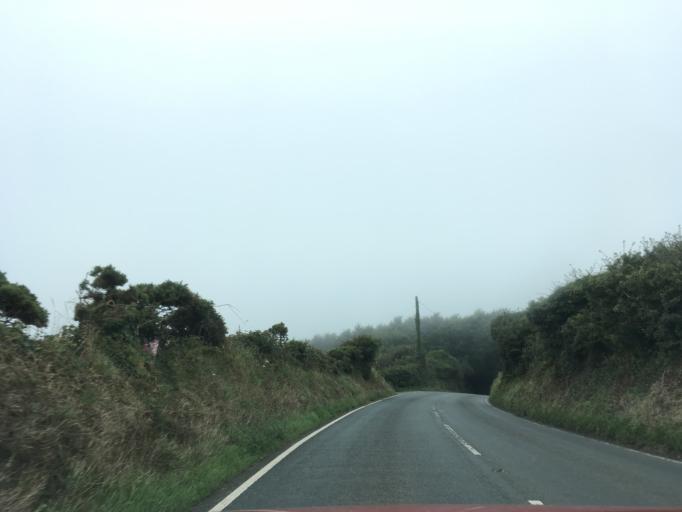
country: GB
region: Wales
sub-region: Pembrokeshire
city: Saint David's
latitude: 51.8781
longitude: -5.2140
